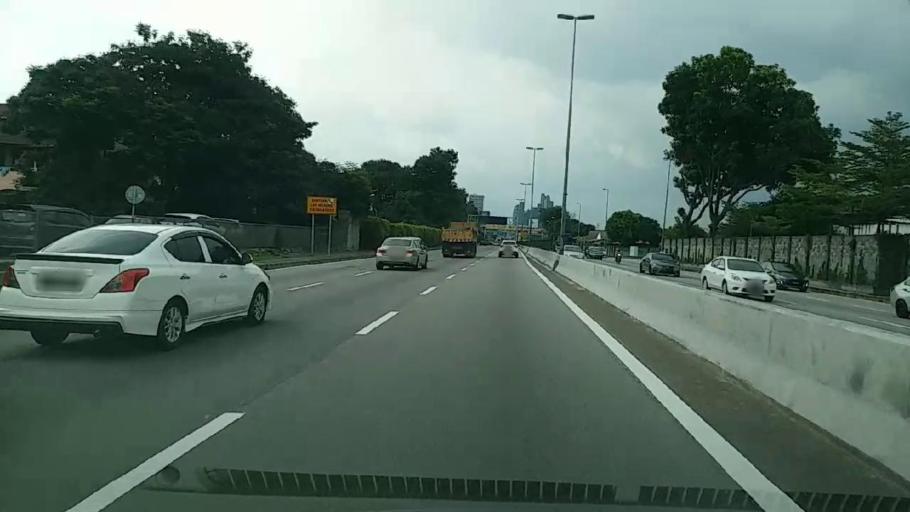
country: MY
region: Selangor
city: Subang Jaya
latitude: 3.0664
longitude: 101.6136
